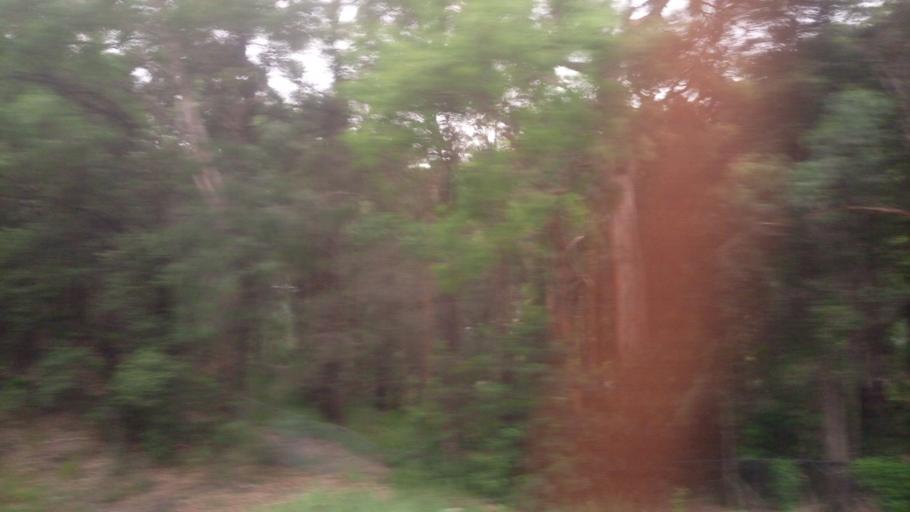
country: AU
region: New South Wales
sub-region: Blue Mountains Municipality
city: Glenbrook
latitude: -33.7707
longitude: 150.6230
